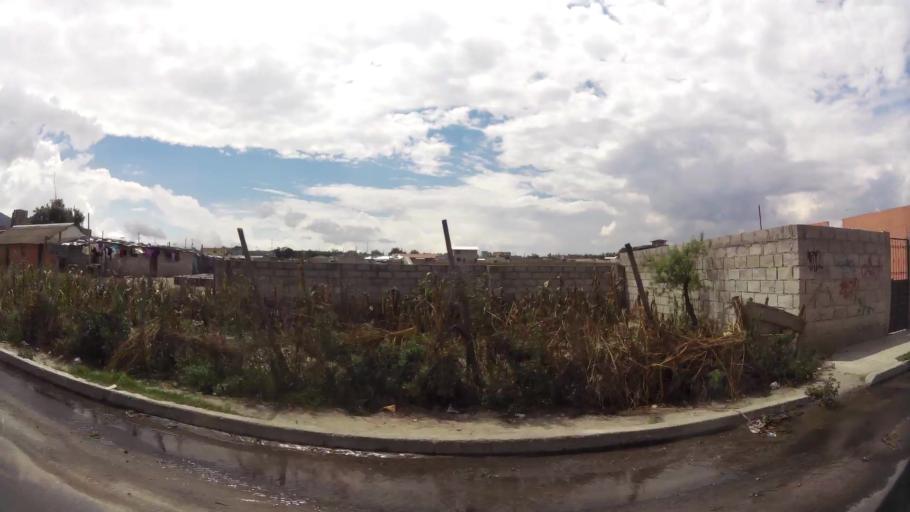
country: EC
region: Pichincha
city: Quito
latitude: -0.0634
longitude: -78.4239
